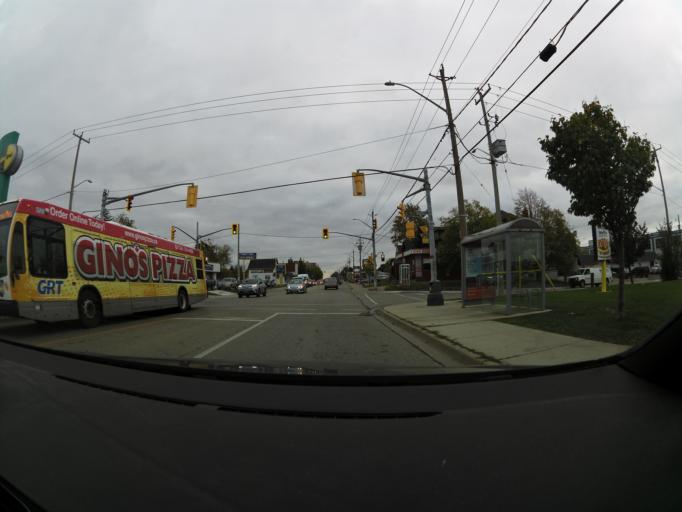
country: CA
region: Ontario
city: Kitchener
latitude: 43.4429
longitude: -80.4741
